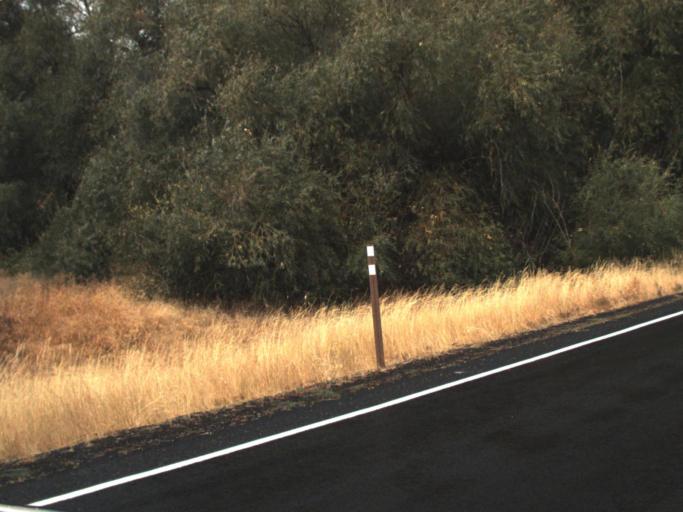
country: US
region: Washington
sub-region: Spokane County
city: Medical Lake
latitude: 47.6867
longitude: -117.8814
